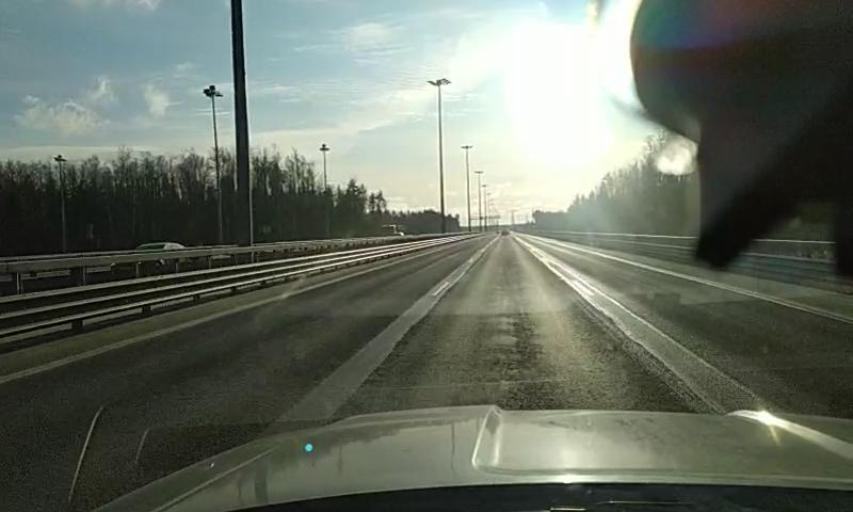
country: RU
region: St.-Petersburg
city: Pesochnyy
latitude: 60.0966
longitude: 30.0936
